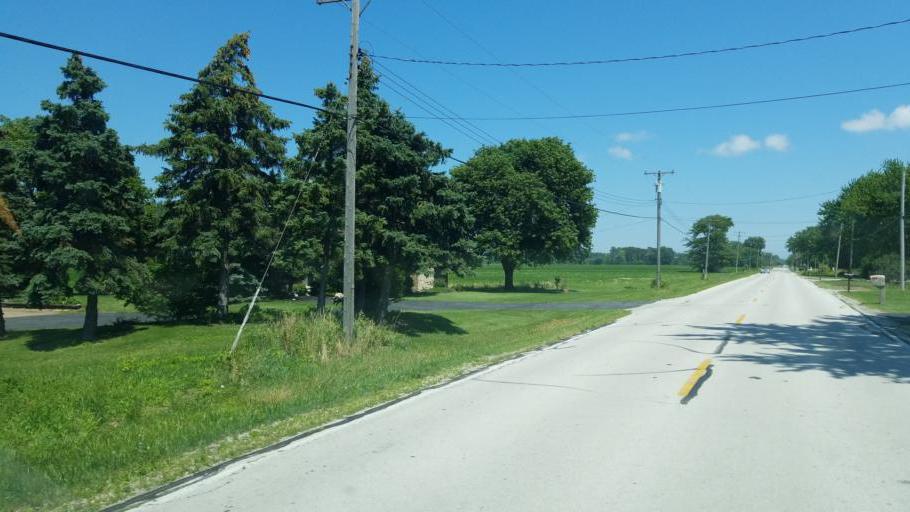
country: US
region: Ohio
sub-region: Ottawa County
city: Port Clinton
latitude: 41.4941
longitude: -82.9266
